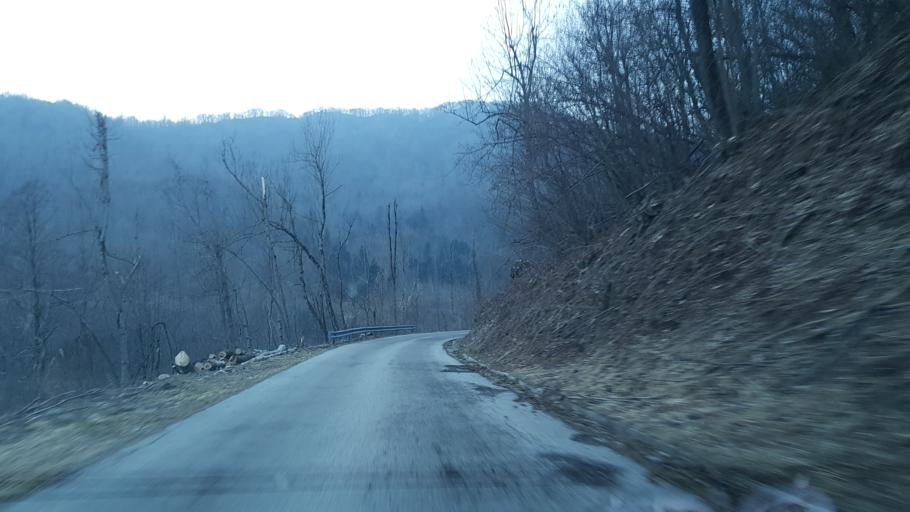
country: IT
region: Friuli Venezia Giulia
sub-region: Provincia di Udine
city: Taipana
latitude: 46.2116
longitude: 13.3595
